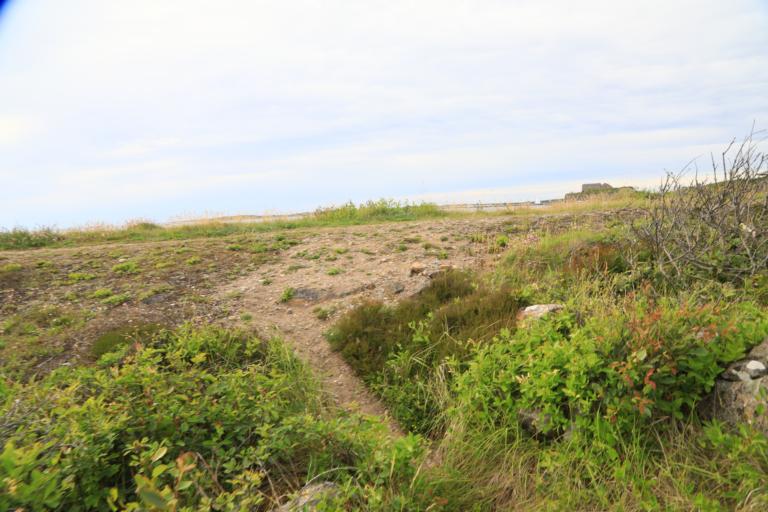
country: SE
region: Halland
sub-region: Varbergs Kommun
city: Varberg
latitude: 57.0957
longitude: 12.2431
